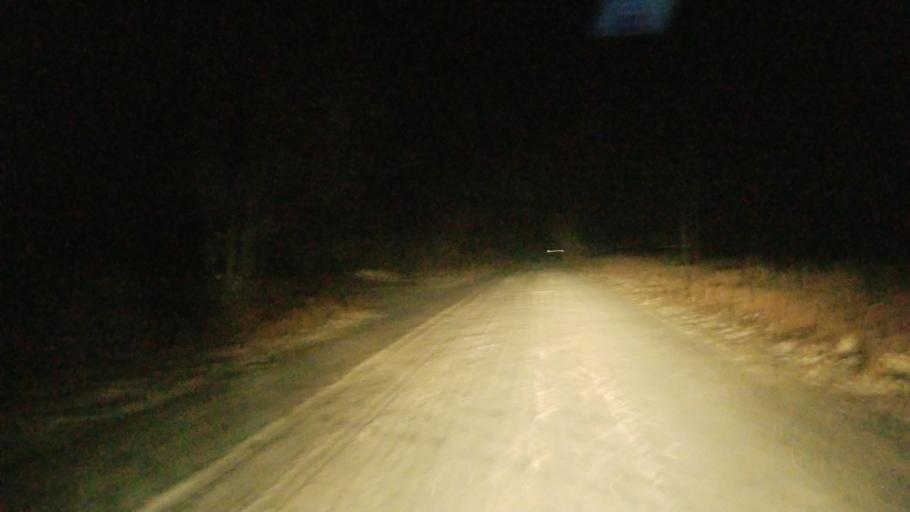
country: US
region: Michigan
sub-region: Osceola County
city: Reed City
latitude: 43.8329
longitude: -85.4141
